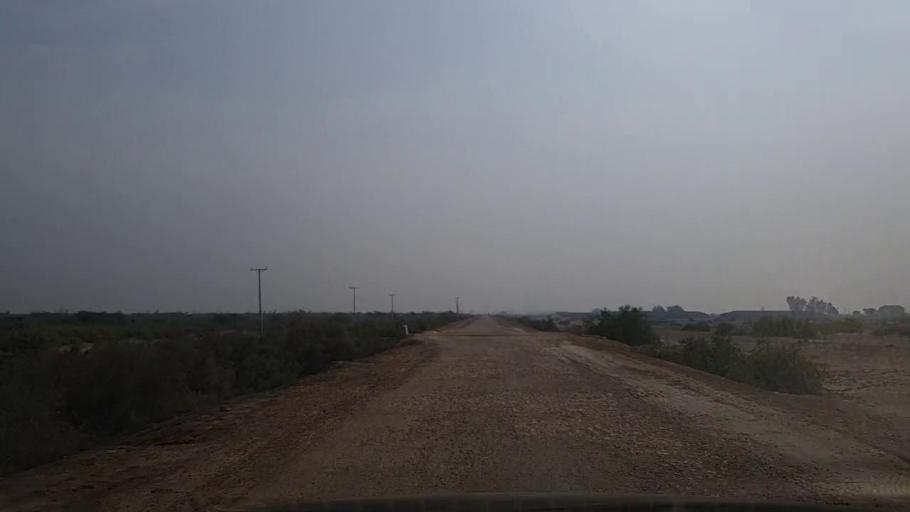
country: PK
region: Sindh
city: Mirpur Sakro
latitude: 24.3922
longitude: 67.7514
